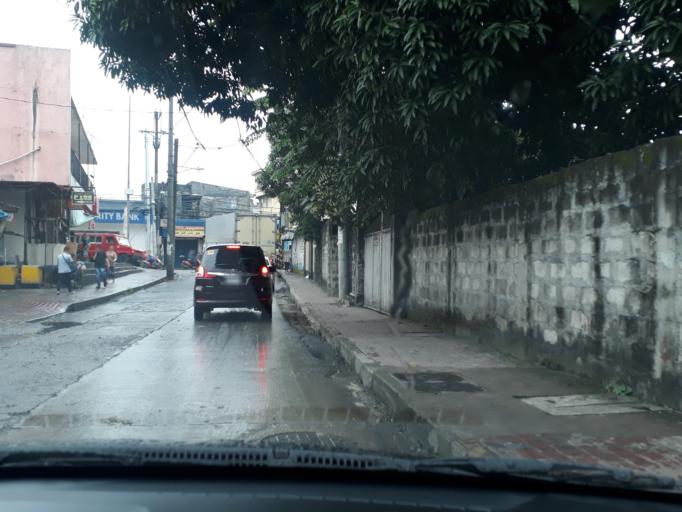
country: PH
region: Calabarzon
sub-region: Province of Rizal
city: Valenzuela
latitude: 14.7076
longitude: 120.9908
